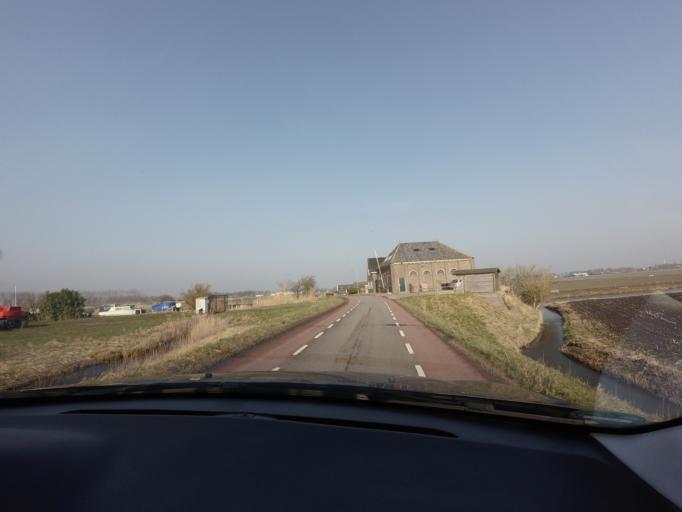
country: NL
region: North Holland
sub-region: Gemeente Beemster
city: Halfweg
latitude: 52.6089
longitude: 4.9595
